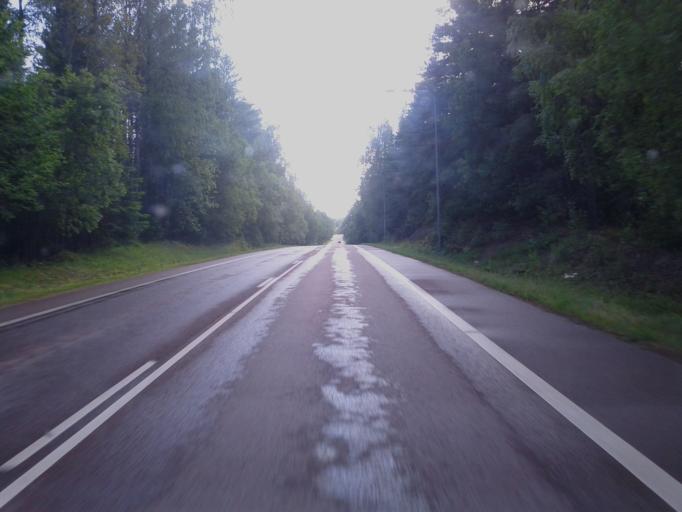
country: SE
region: Dalarna
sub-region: Borlange Kommun
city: Ornas
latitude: 60.5037
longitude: 15.5052
